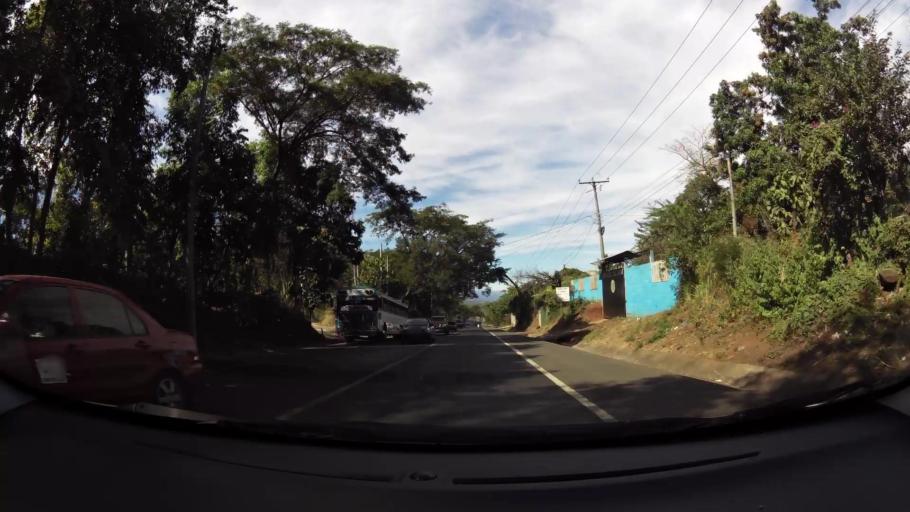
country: SV
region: San Salvador
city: Guazapa
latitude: 13.9165
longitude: -89.1830
